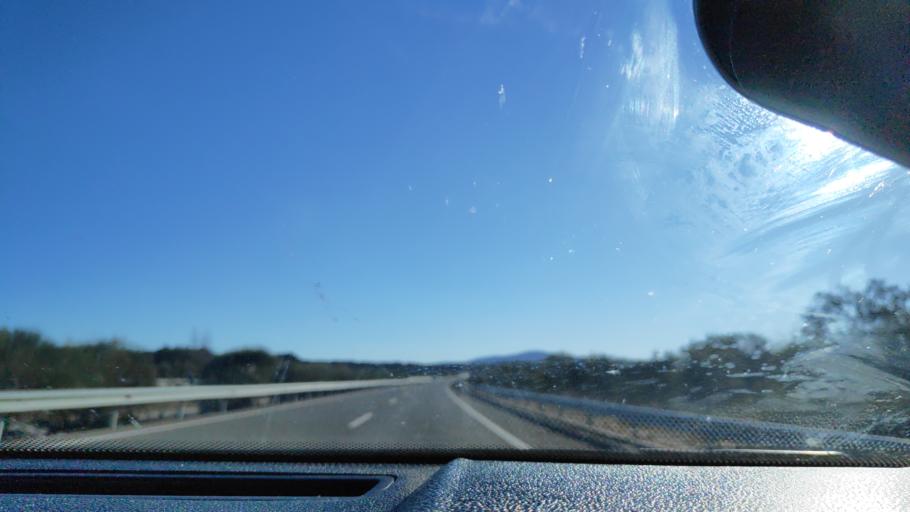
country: ES
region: Andalusia
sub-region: Provincia de Huelva
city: Cala
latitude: 37.9844
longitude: -6.2331
